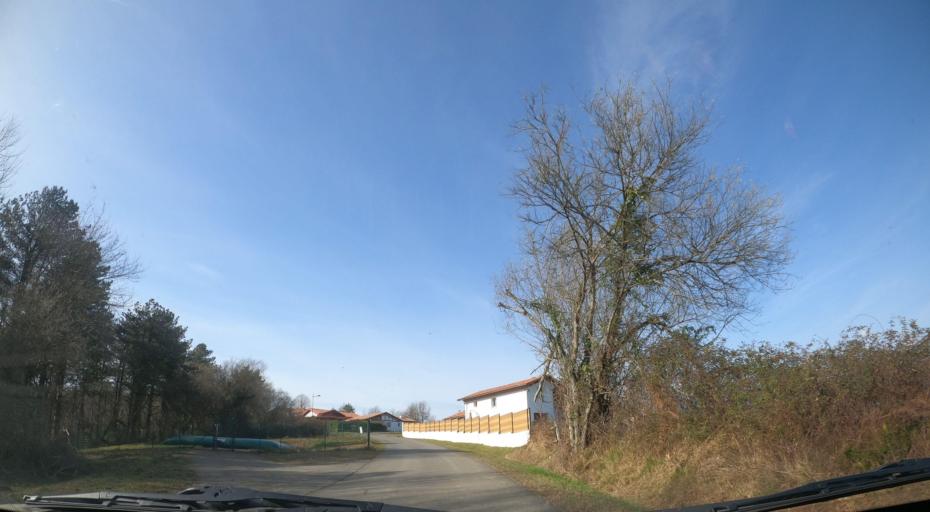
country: FR
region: Aquitaine
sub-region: Departement des Pyrenees-Atlantiques
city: Briscous
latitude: 43.4272
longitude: -1.3726
